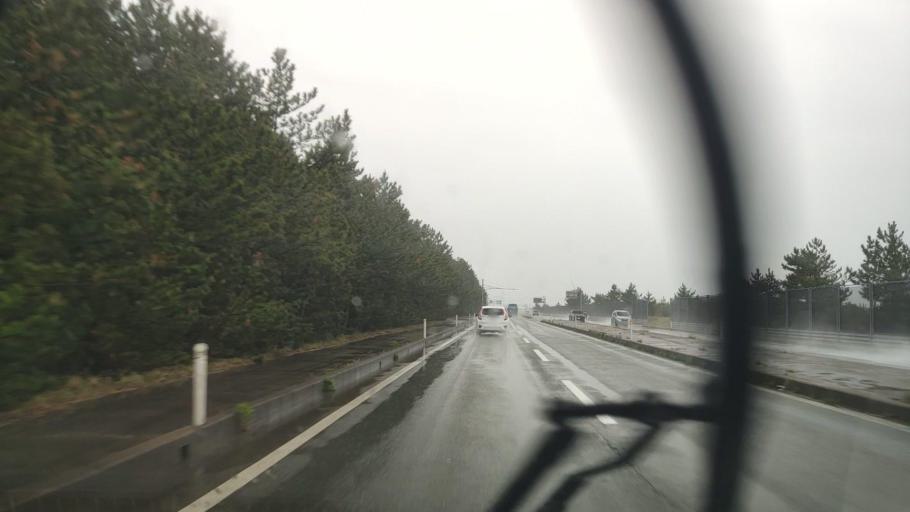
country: JP
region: Akita
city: Akita Shi
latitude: 39.7782
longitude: 140.0447
